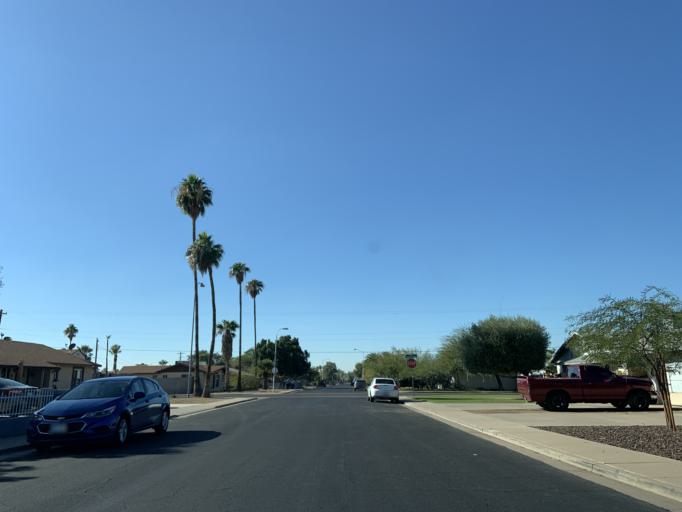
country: US
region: Arizona
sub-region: Maricopa County
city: Tempe
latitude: 33.4058
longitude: -111.8651
